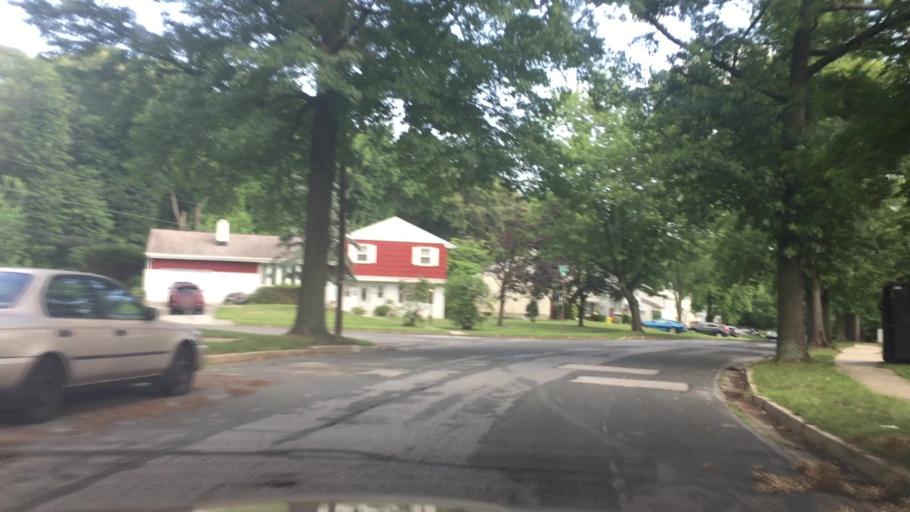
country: US
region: Maryland
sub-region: Anne Arundel County
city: South Gate
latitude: 39.1379
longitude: -76.6410
